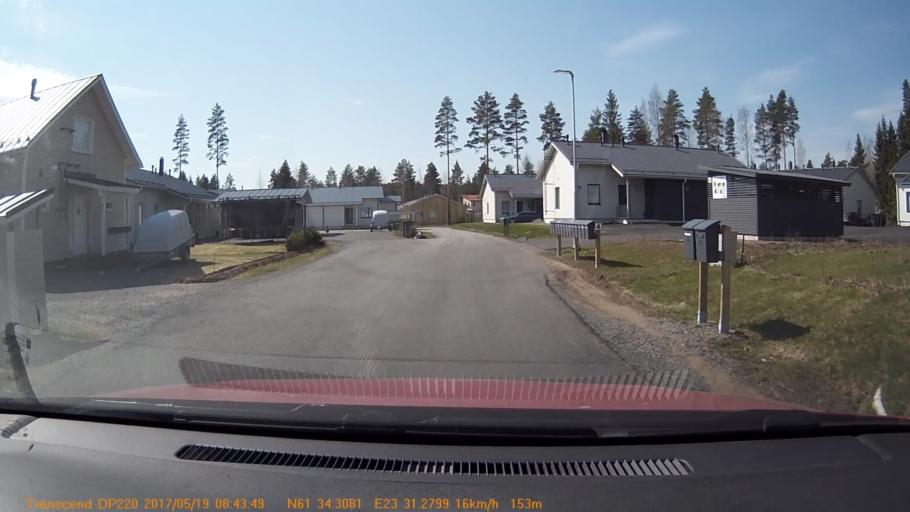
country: FI
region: Pirkanmaa
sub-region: Tampere
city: Yloejaervi
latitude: 61.5717
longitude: 23.5211
